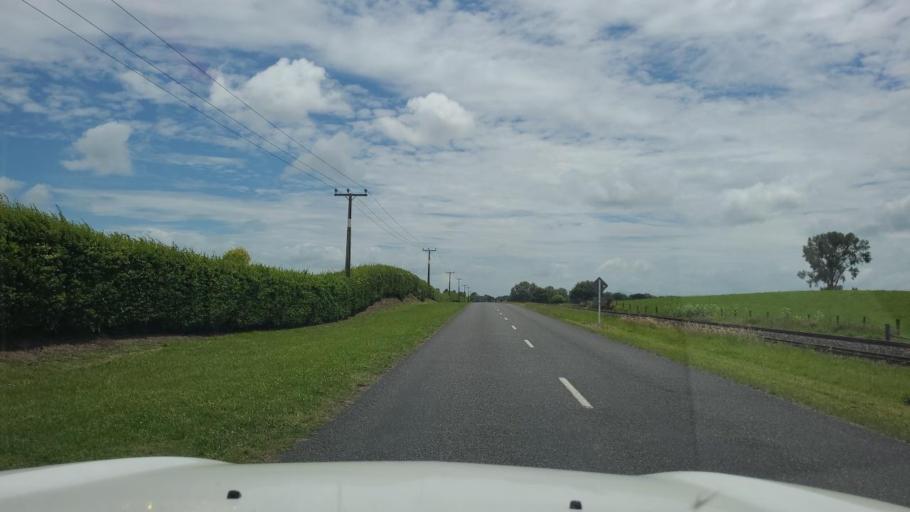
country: NZ
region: Waikato
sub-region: Matamata-Piako District
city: Matamata
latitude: -37.8775
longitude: 175.7585
